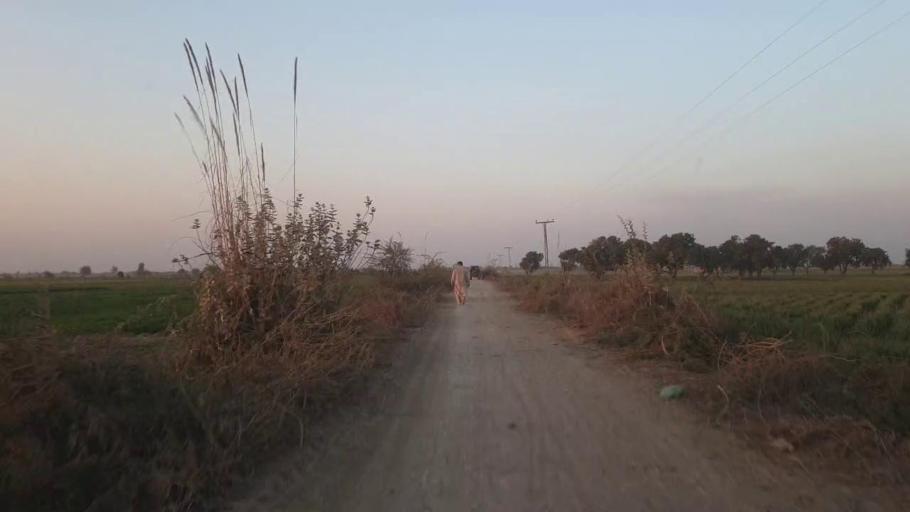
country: PK
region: Sindh
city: Chambar
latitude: 25.3001
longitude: 68.9075
